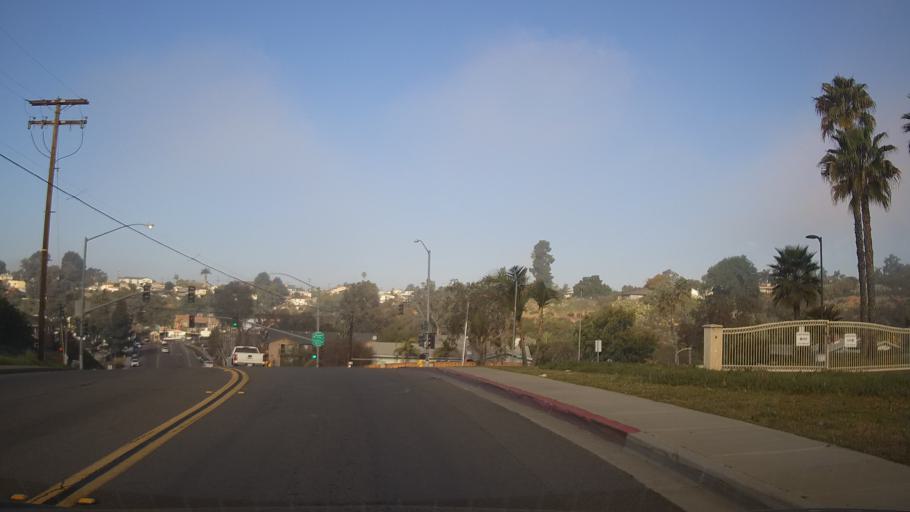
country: US
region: California
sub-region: San Diego County
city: Lemon Grove
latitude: 32.7368
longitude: -117.0893
